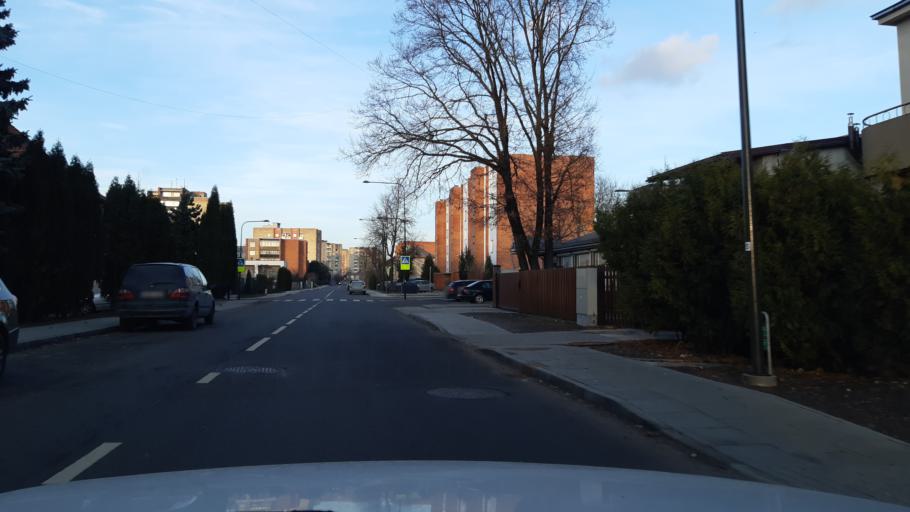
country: LT
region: Kauno apskritis
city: Dainava (Kaunas)
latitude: 54.8879
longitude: 23.9410
